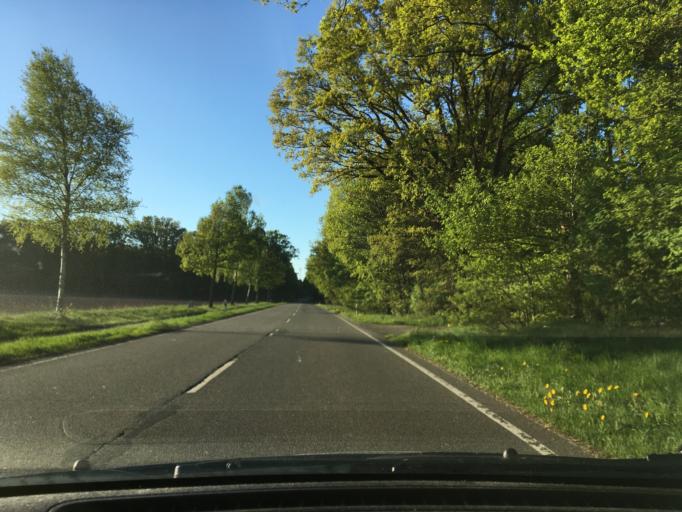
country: DE
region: Lower Saxony
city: Bispingen
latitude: 53.0317
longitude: 9.9997
